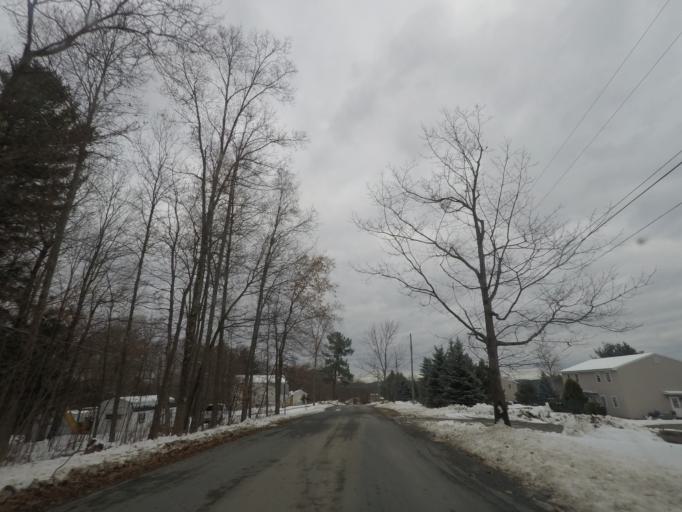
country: US
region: New York
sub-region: Rensselaer County
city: West Sand Lake
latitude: 42.6102
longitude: -73.6320
